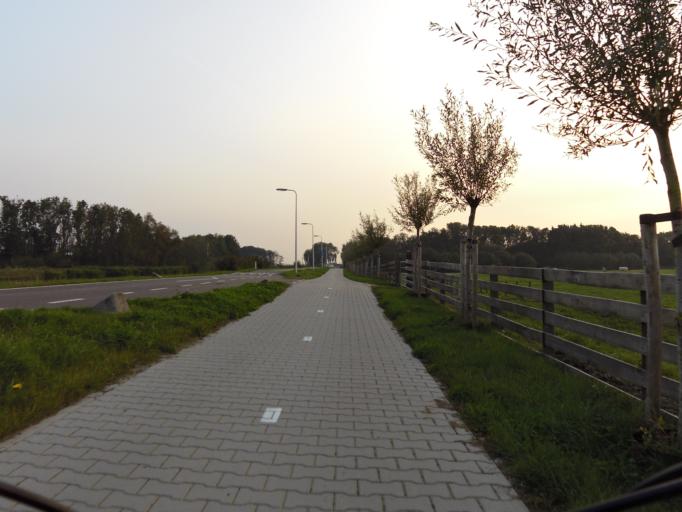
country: NL
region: South Holland
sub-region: Gemeente Zoetermeer
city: Zoetermeer
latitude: 52.1026
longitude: 4.5019
